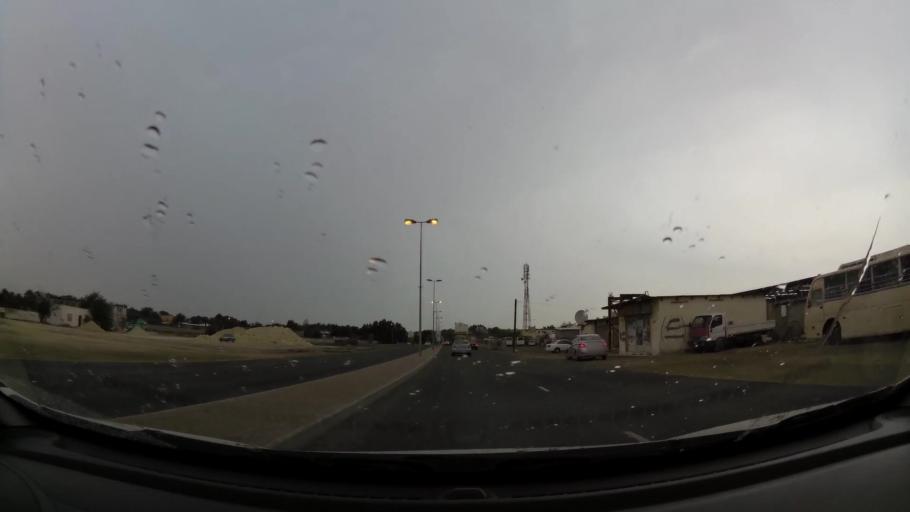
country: BH
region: Central Governorate
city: Madinat Hamad
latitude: 26.1126
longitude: 50.4844
